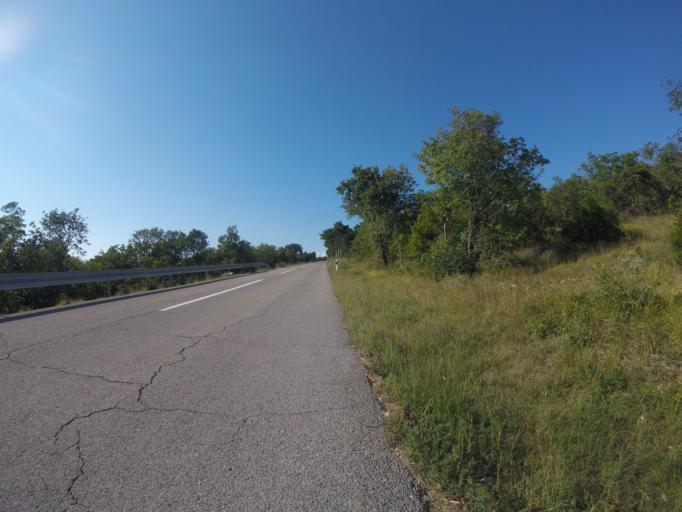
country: HR
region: Primorsko-Goranska
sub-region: Grad Crikvenica
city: Jadranovo
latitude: 45.2521
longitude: 14.6068
